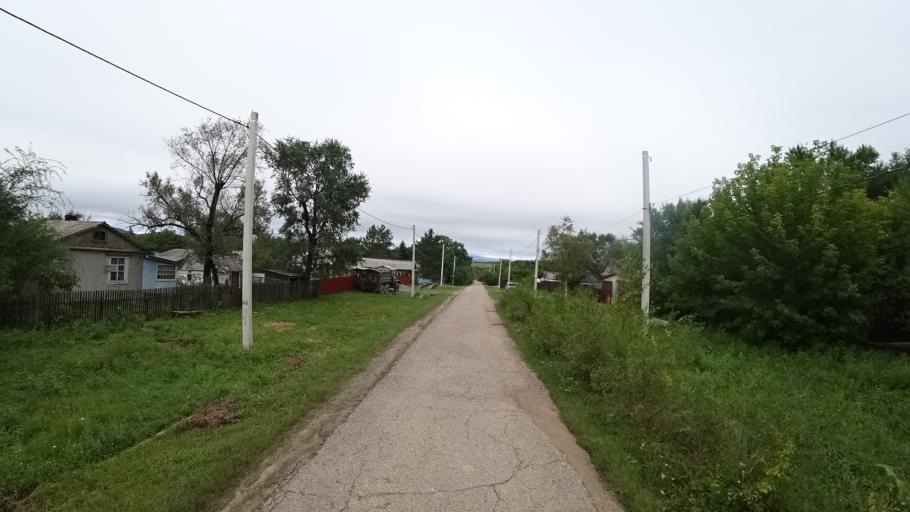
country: RU
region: Primorskiy
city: Monastyrishche
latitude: 44.0807
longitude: 132.5870
